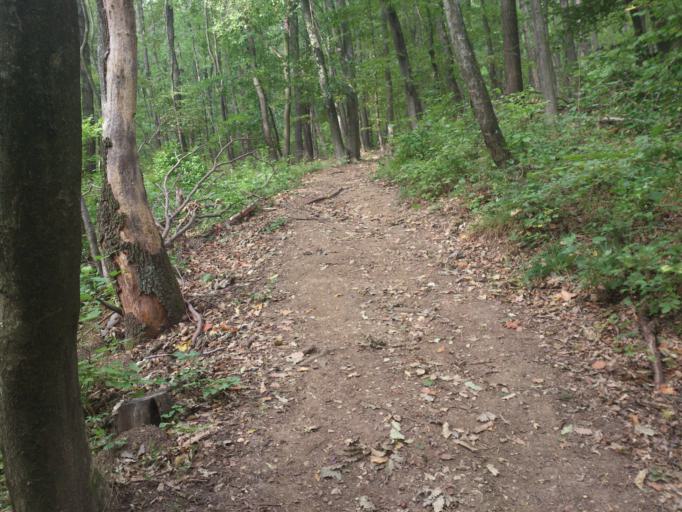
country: HU
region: Pest
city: Pilisszanto
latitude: 47.6844
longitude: 18.8811
